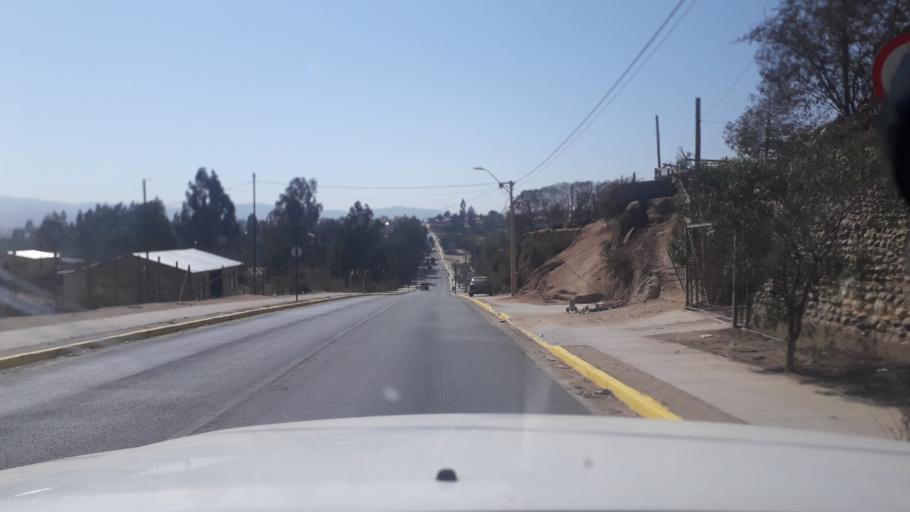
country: CL
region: Valparaiso
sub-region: Provincia de Marga Marga
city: Villa Alemana
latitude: -33.0702
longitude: -71.4044
